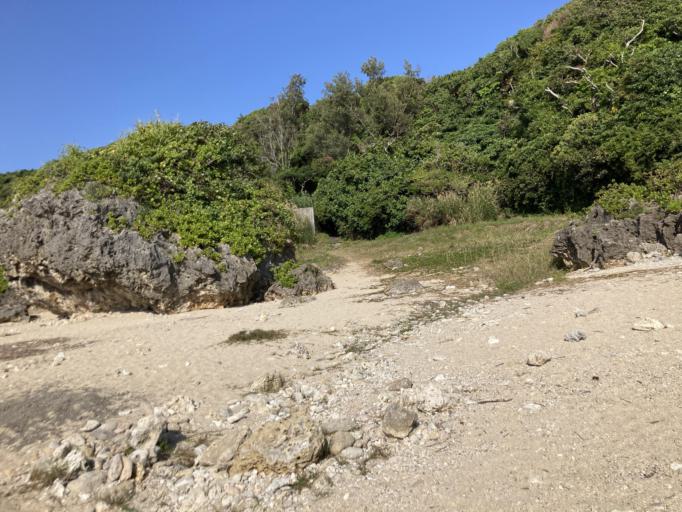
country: JP
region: Okinawa
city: Itoman
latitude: 26.1186
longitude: 127.7475
